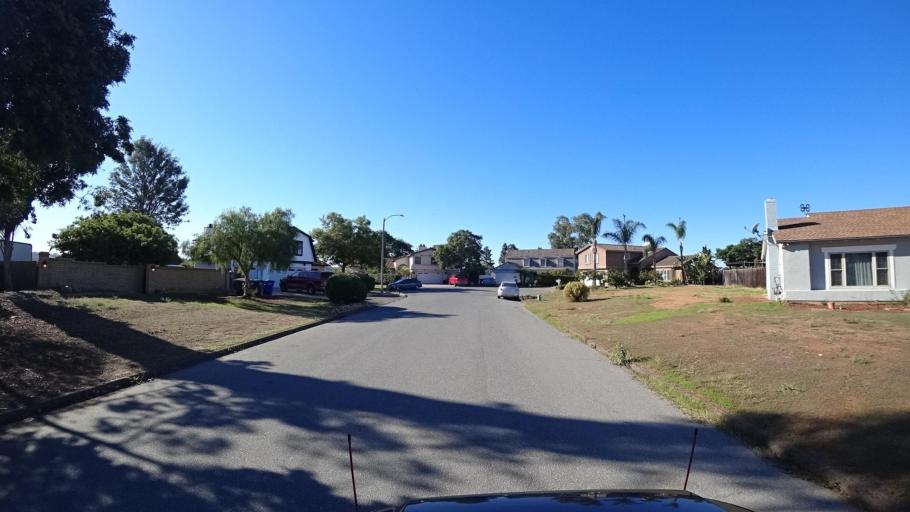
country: US
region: California
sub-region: San Diego County
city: Bonita
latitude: 32.6808
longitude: -117.0190
